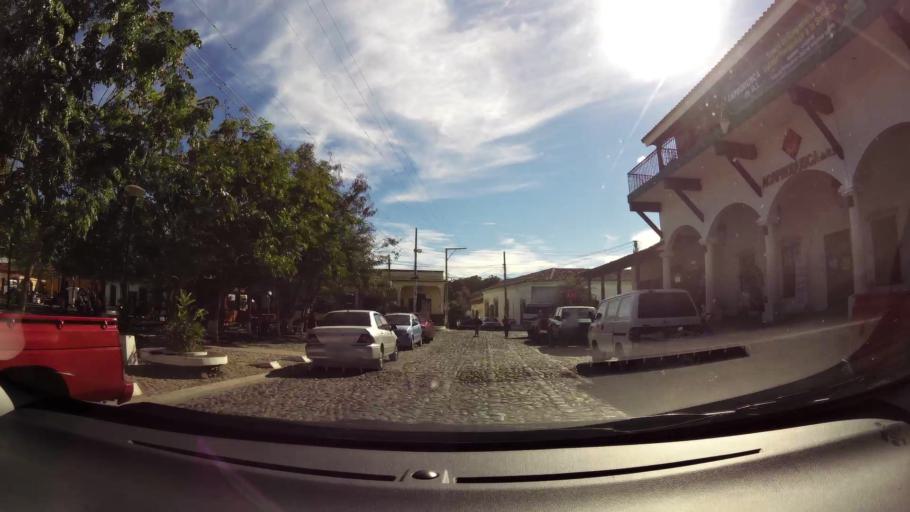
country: SV
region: Cuscatlan
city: Suchitoto
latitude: 13.9370
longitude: -89.0263
